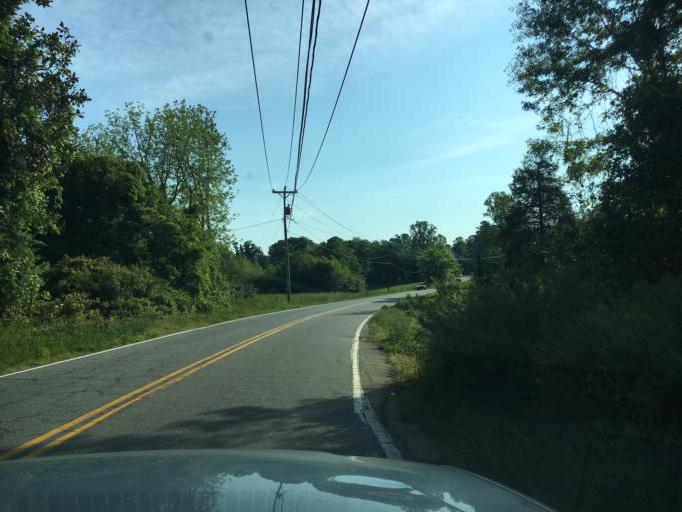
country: US
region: North Carolina
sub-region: Rutherford County
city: Rutherfordton
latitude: 35.3771
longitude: -81.9664
